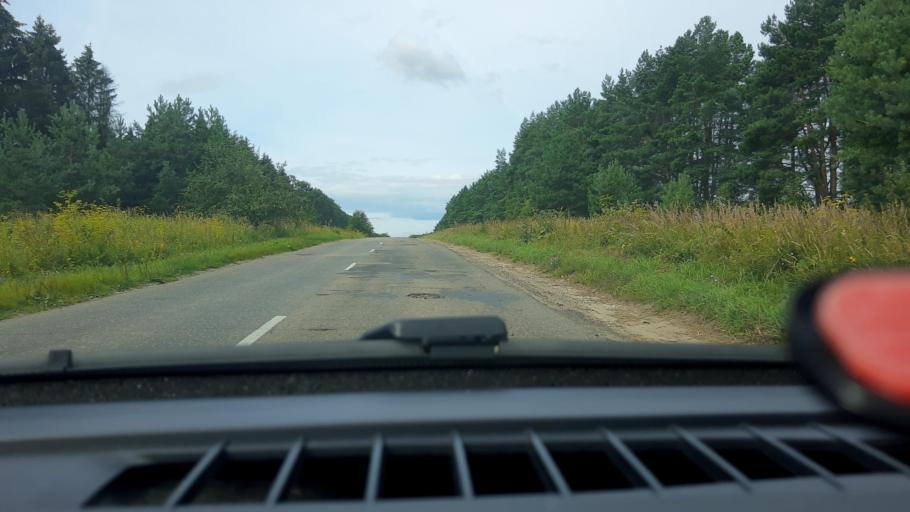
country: RU
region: Nizjnij Novgorod
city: Bogorodsk
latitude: 56.0666
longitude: 43.6386
